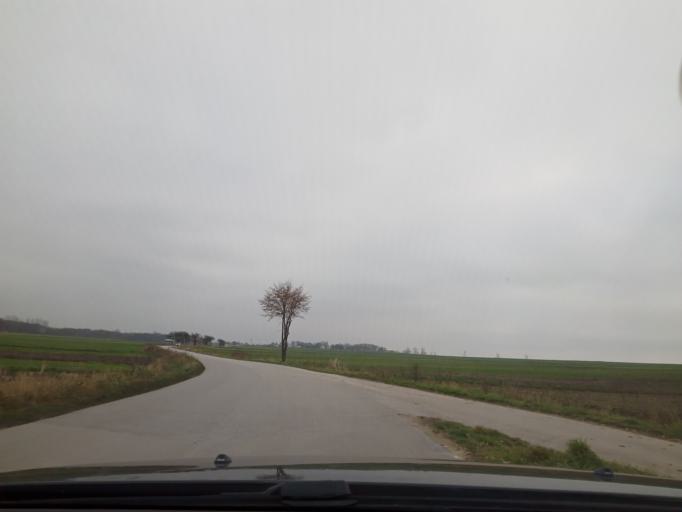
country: PL
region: Swietokrzyskie
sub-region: Powiat jedrzejowski
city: Imielno
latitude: 50.5905
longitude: 20.4263
